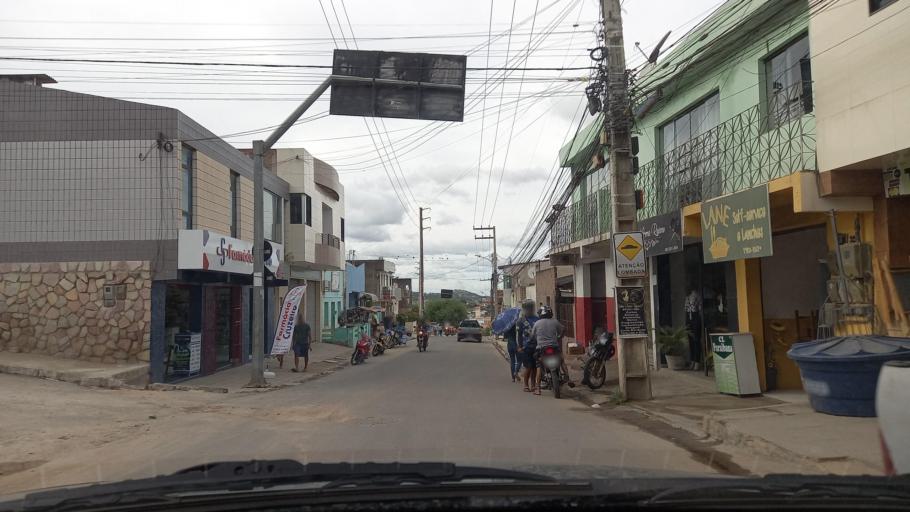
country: BR
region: Pernambuco
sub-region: Gravata
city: Gravata
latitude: -8.2108
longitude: -35.5716
